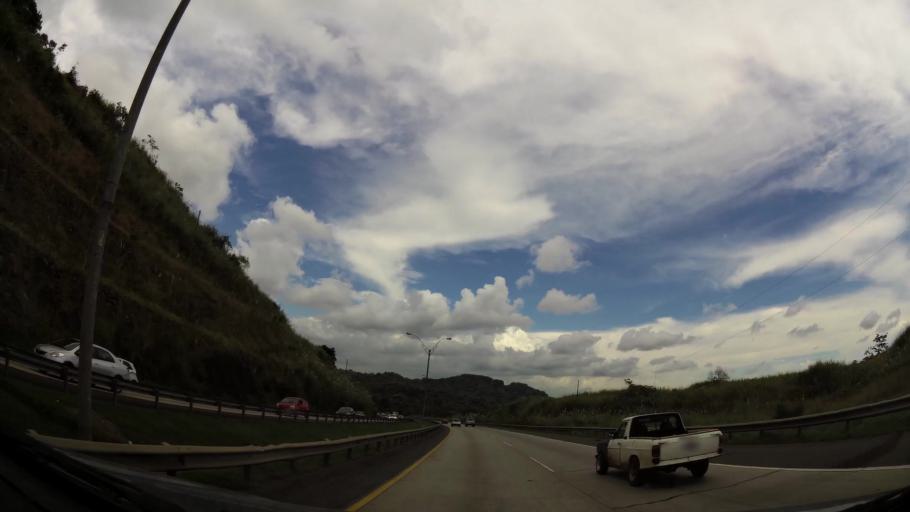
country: PA
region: Panama
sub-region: Distrito Arraijan
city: Arraijan
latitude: 8.9662
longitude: -79.6461
